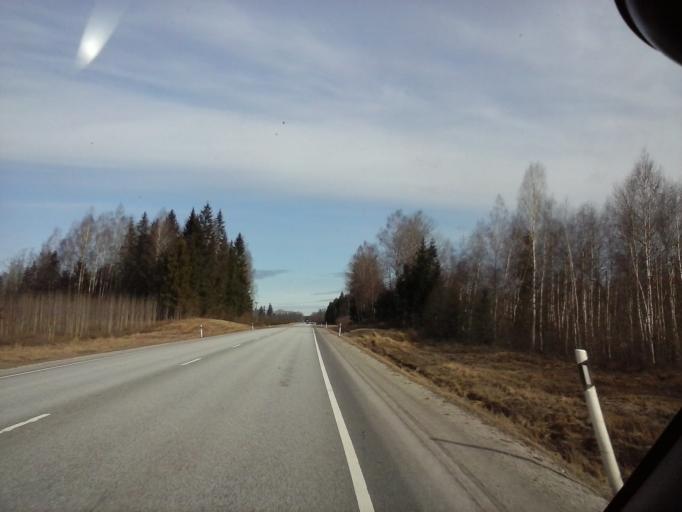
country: EE
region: Jaervamaa
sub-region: Paide linn
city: Paide
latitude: 58.9543
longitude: 25.6087
